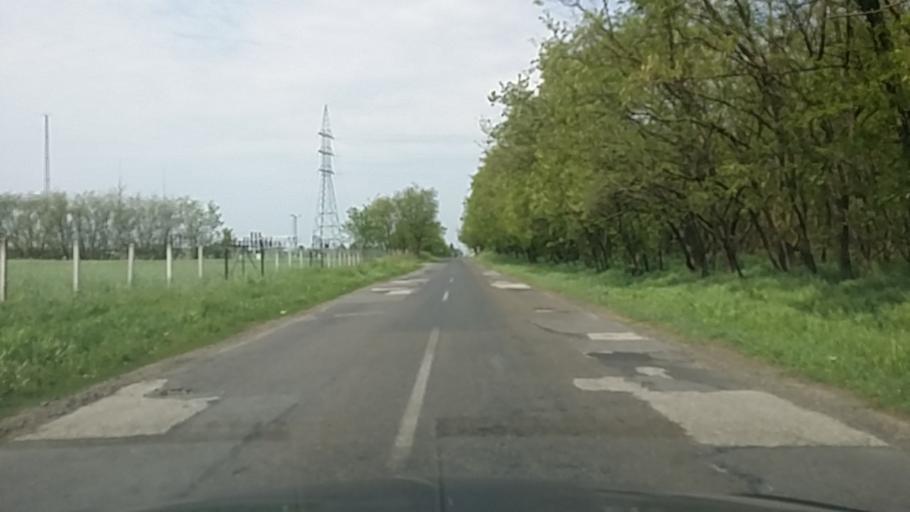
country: HU
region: Szabolcs-Szatmar-Bereg
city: Nyirbogdany
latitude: 48.0716
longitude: 21.8599
